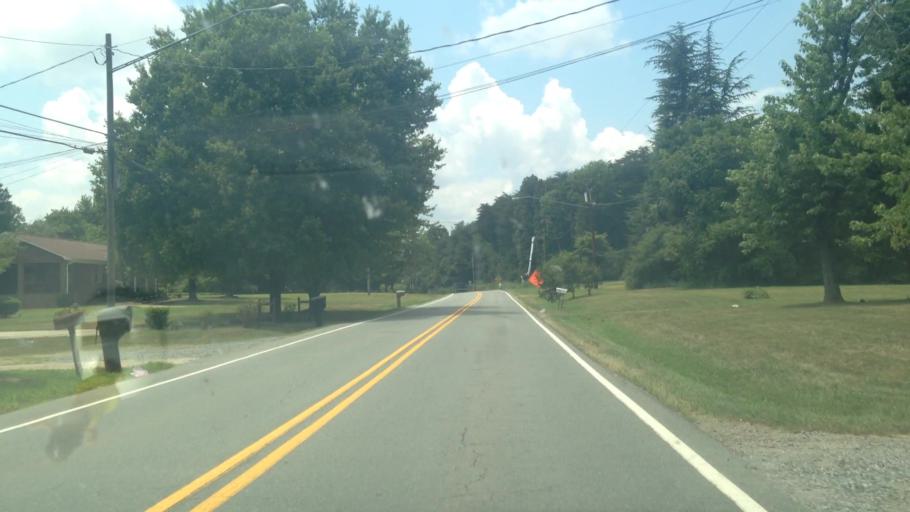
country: US
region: North Carolina
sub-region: Forsyth County
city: Rural Hall
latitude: 36.1941
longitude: -80.2504
